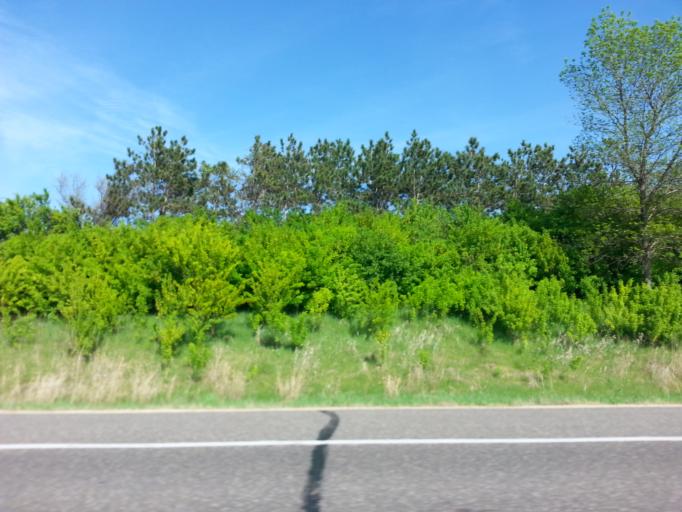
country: US
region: Minnesota
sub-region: Washington County
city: Oakdale
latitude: 44.9846
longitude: -92.9340
